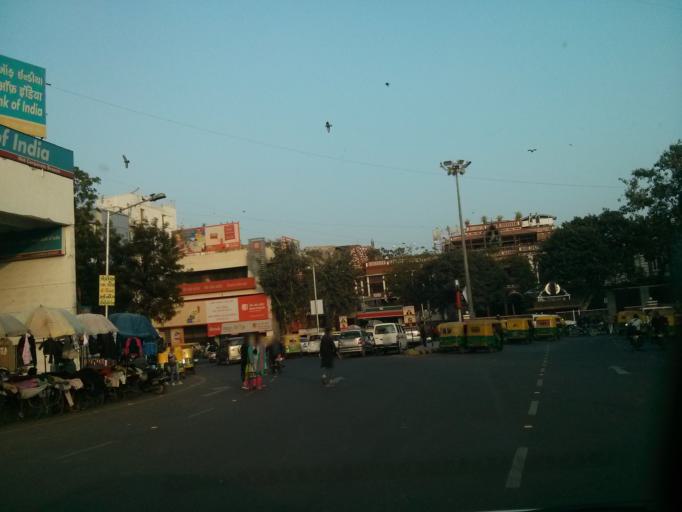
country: IN
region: Gujarat
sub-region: Ahmadabad
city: Ahmedabad
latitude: 23.0274
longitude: 72.5808
